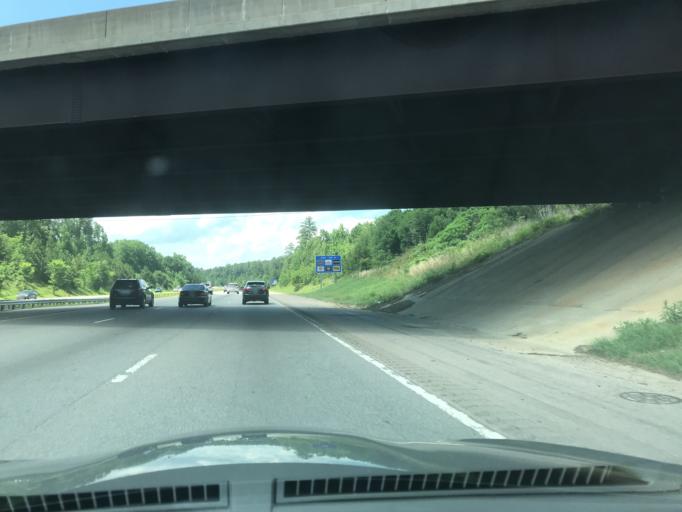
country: US
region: North Carolina
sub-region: Wake County
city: Raleigh
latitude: 35.8836
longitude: -78.5904
